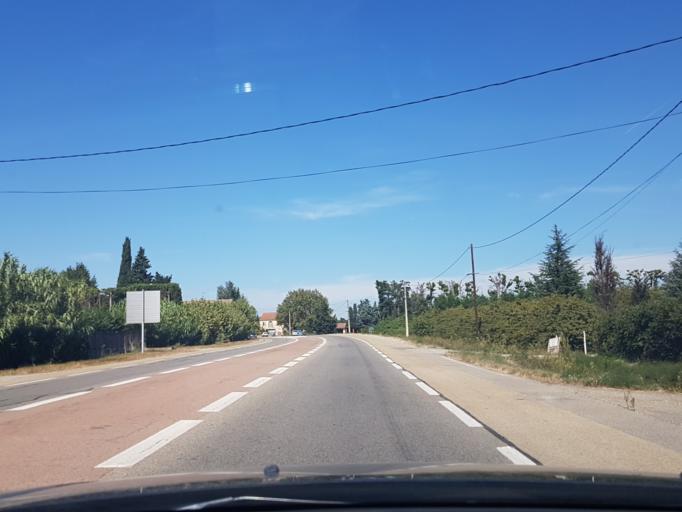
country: FR
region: Provence-Alpes-Cote d'Azur
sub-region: Departement des Bouches-du-Rhone
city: Rognonas
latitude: 43.9011
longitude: 4.8172
